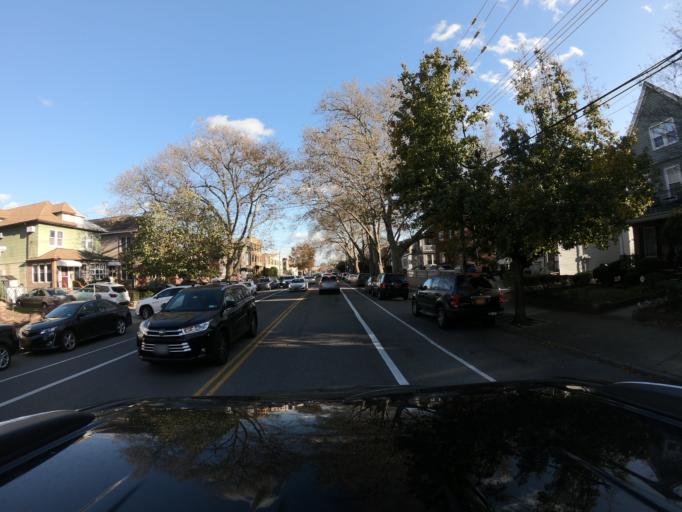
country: US
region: New York
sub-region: Kings County
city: Bensonhurst
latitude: 40.6213
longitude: -74.0092
